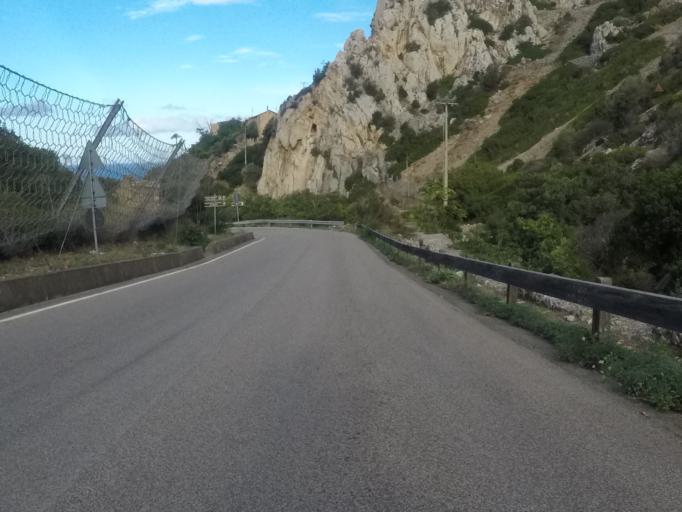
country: IT
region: Sardinia
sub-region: Provincia di Carbonia-Iglesias
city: Buggerru
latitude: 39.3317
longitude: 8.4358
